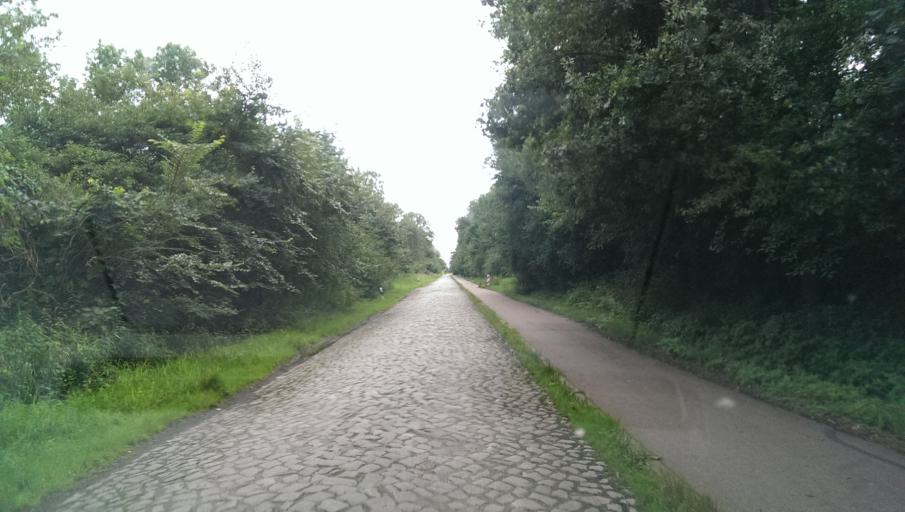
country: DE
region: Saxony-Anhalt
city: Worlitz
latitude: 51.8614
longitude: 12.4368
